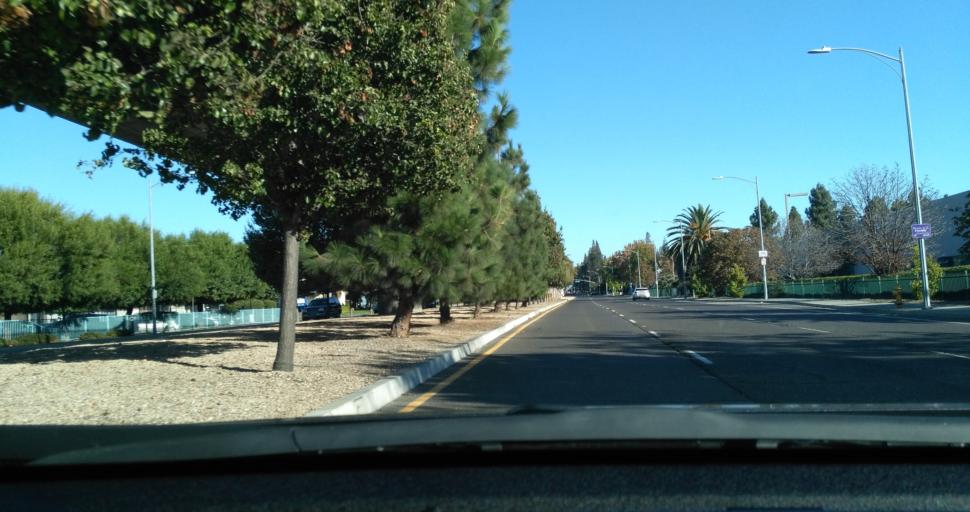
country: US
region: California
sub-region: Santa Clara County
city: Milpitas
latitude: 37.4066
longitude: -121.8875
